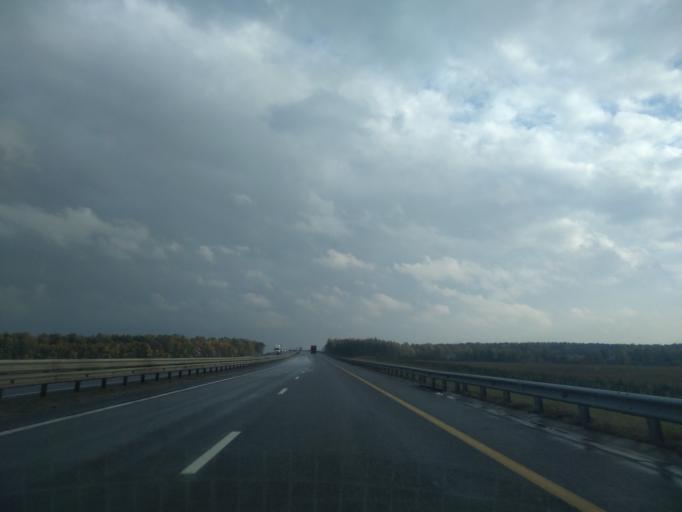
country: RU
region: Lipetsk
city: Yelets
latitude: 52.5998
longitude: 38.6697
